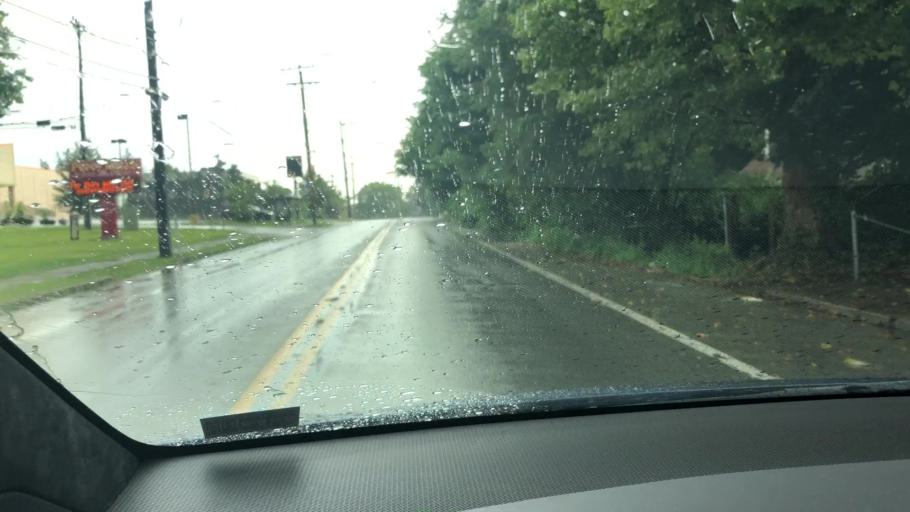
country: US
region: Pennsylvania
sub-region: Allegheny County
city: Penn Hills
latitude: 40.4708
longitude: -79.8204
